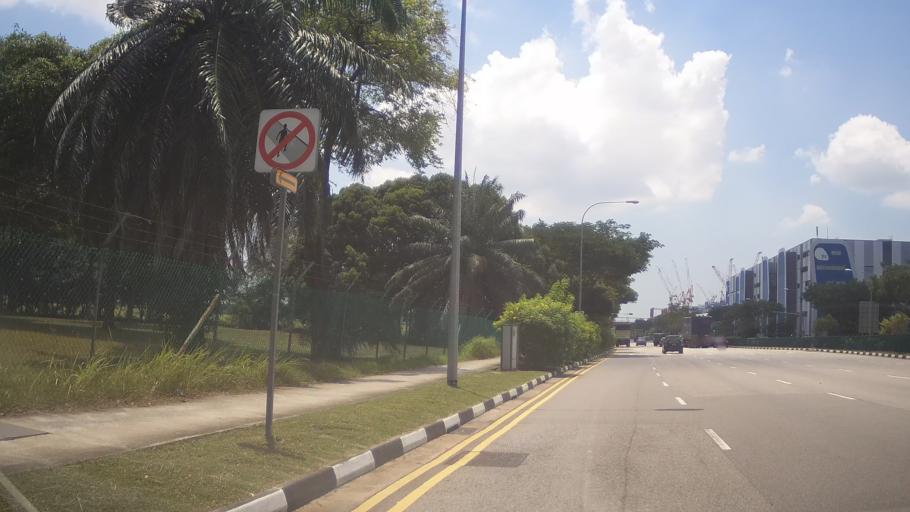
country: MY
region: Johor
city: Johor Bahru
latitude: 1.3220
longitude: 103.6793
